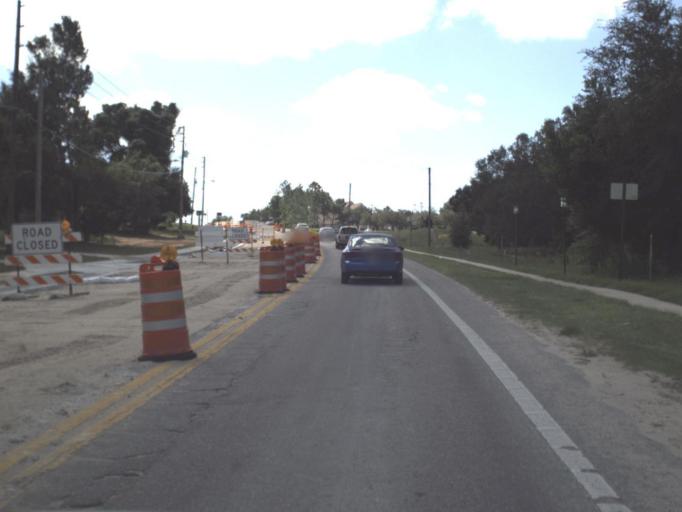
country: US
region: Florida
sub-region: Polk County
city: Haines City
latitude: 28.0882
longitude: -81.6233
